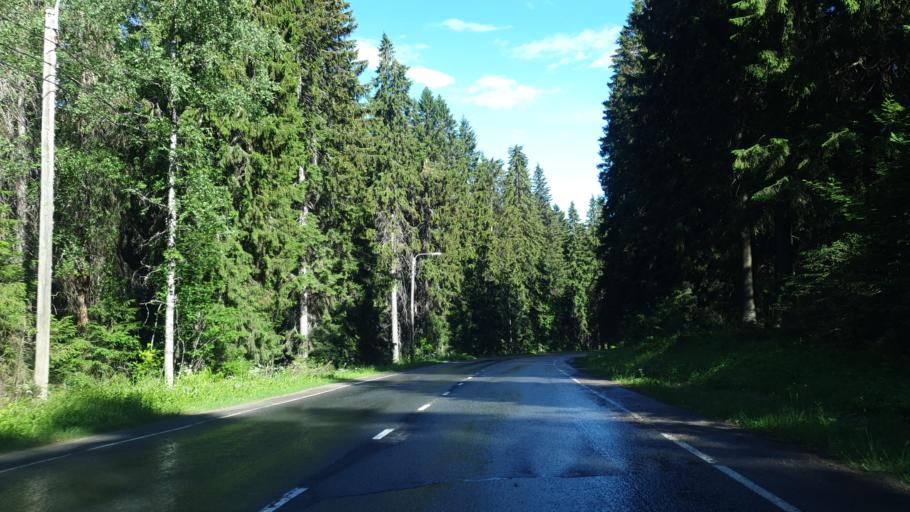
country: FI
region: Northern Savo
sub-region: Kuopio
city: Kuopio
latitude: 62.9086
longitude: 27.6655
